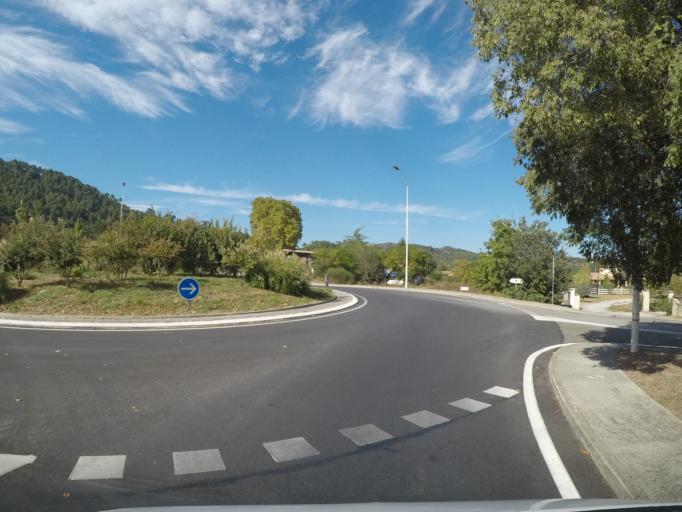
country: FR
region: Languedoc-Roussillon
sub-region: Departement du Gard
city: Anduze
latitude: 44.0657
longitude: 3.9713
